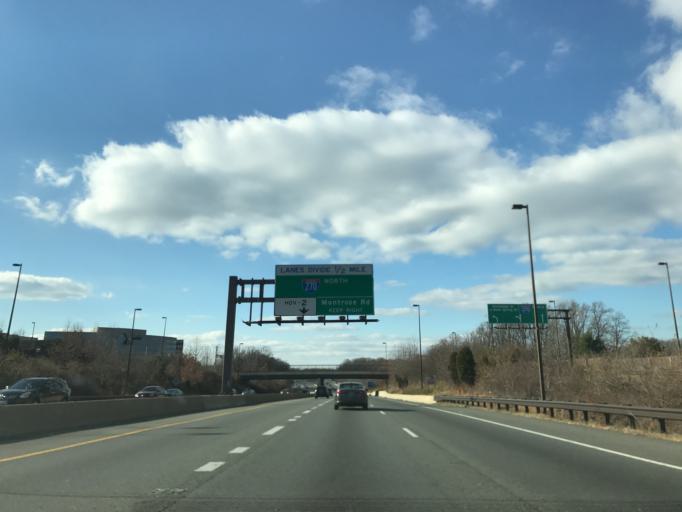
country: US
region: Maryland
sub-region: Montgomery County
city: North Bethesda
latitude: 39.0313
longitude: -77.1292
